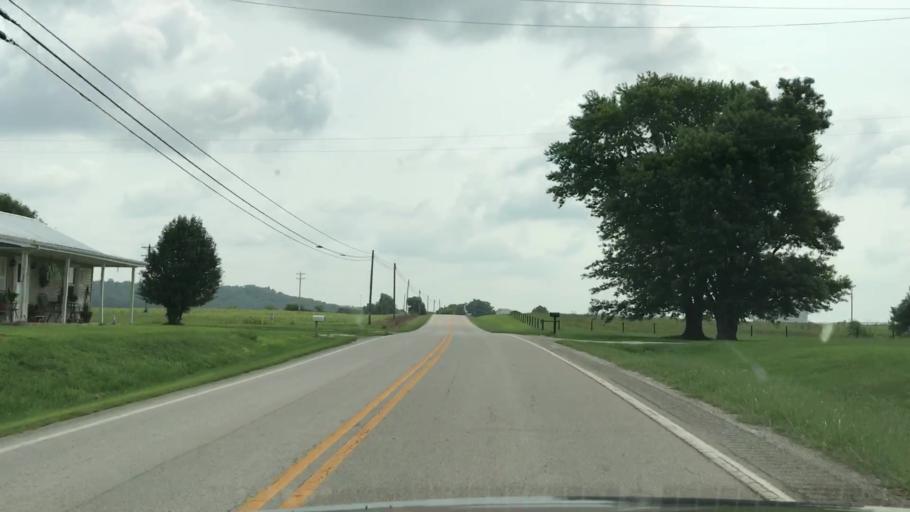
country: US
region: Kentucky
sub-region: Barren County
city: Cave City
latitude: 37.0926
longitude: -86.1016
